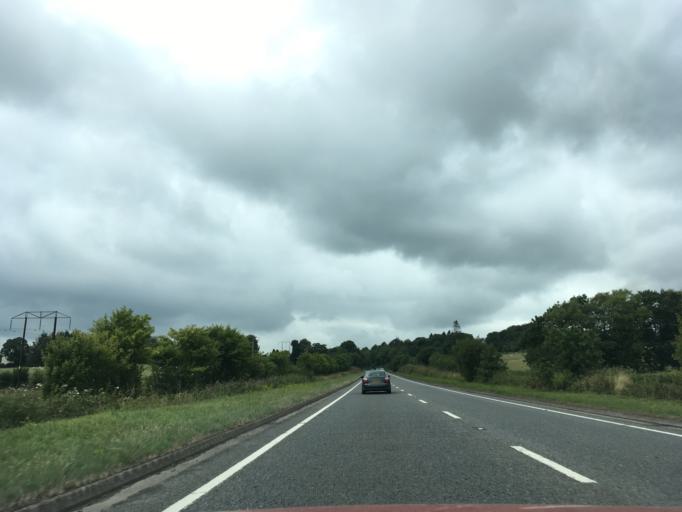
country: GB
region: Wales
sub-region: Carmarthenshire
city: Whitland
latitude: 51.8256
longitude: -4.6101
